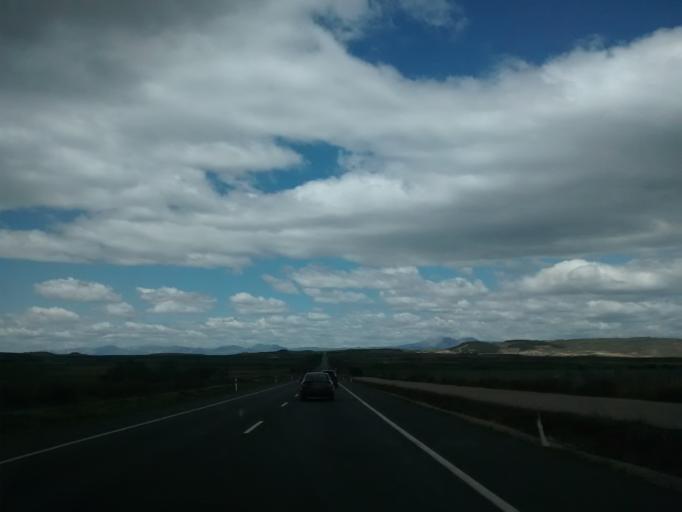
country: ES
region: La Rioja
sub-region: Provincia de La Rioja
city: Ausejo
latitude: 42.3630
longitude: -2.1908
